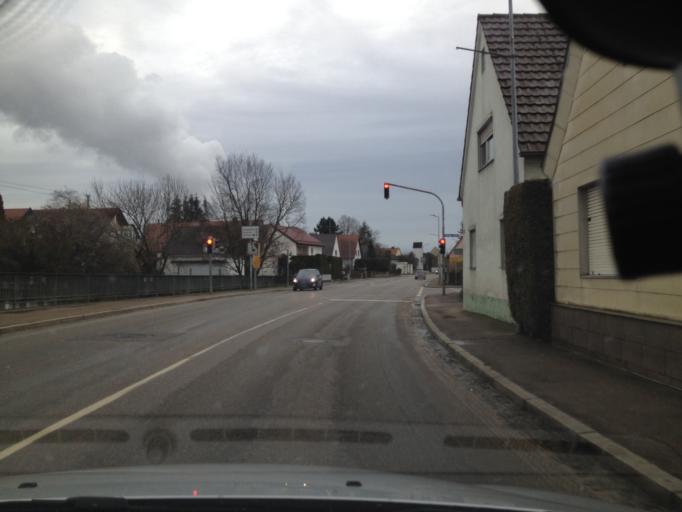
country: DE
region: Bavaria
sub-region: Swabia
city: Gundelfingen
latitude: 48.5496
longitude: 10.3673
